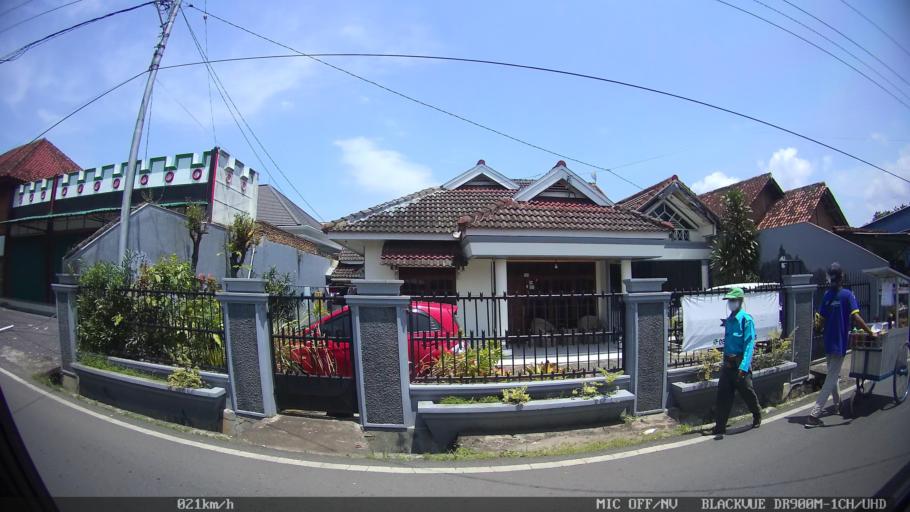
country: ID
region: Lampung
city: Kedaton
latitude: -5.4030
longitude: 105.2633
